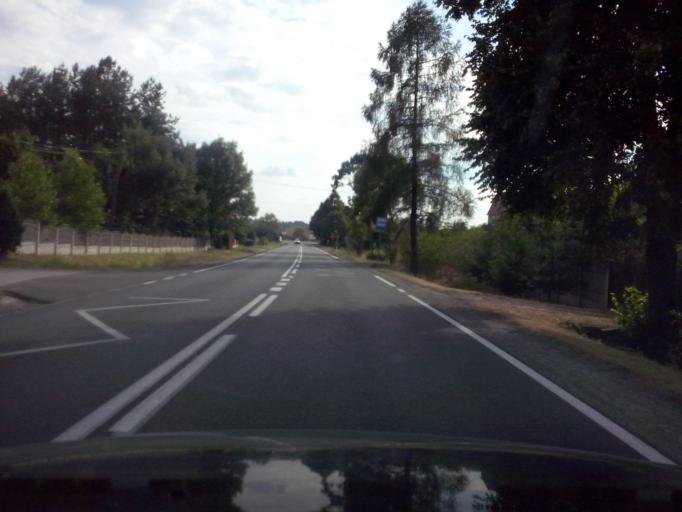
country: PL
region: Swietokrzyskie
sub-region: Powiat kielecki
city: Rakow
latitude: 50.6795
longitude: 21.0502
